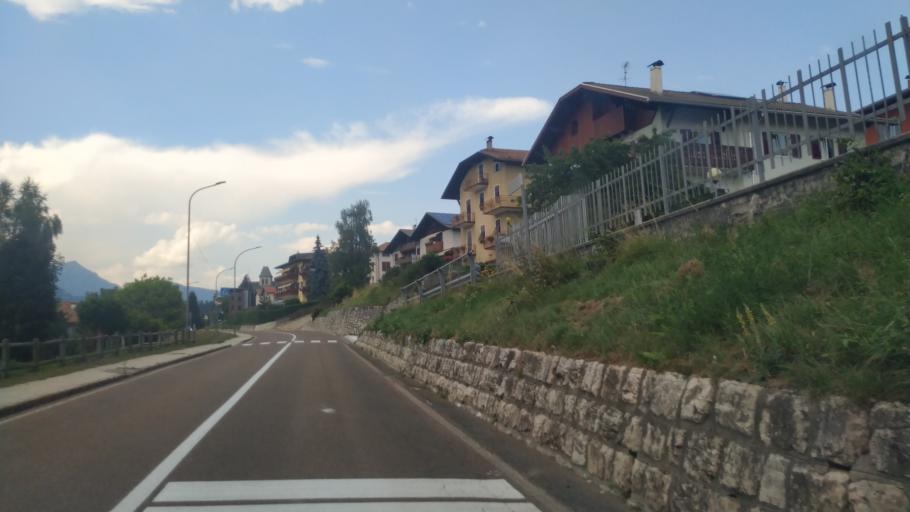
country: IT
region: Trentino-Alto Adige
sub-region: Provincia di Trento
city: Malosco
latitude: 46.4327
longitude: 11.1408
